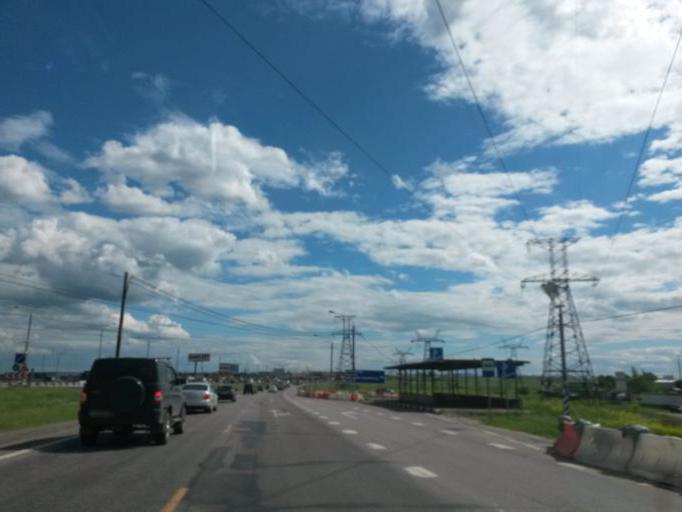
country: RU
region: Moskovskaya
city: Shcherbinka
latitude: 55.4628
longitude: 37.6184
